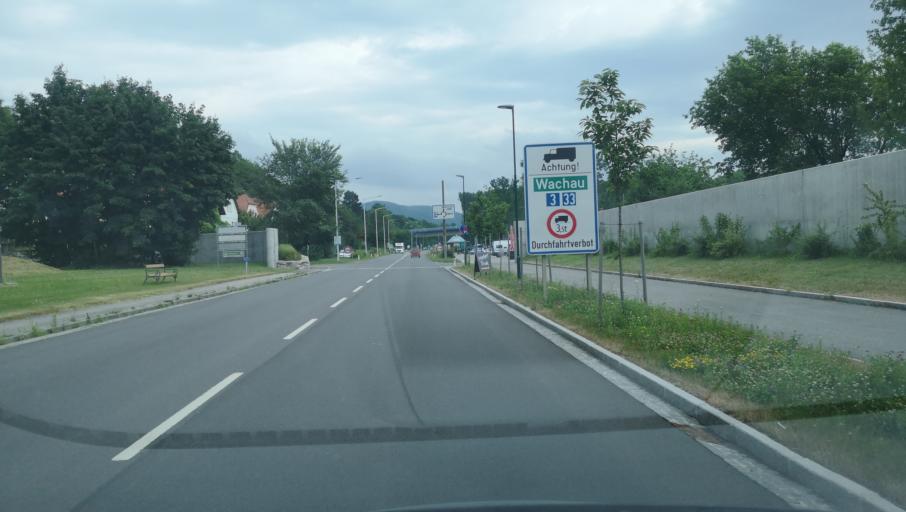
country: AT
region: Lower Austria
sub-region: Politischer Bezirk Melk
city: Emmersdorf an der Donau
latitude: 48.2426
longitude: 15.3395
